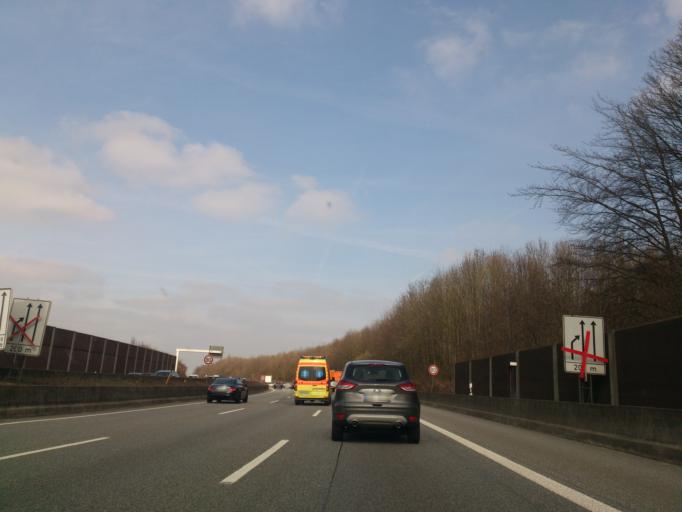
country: DE
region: North Rhine-Westphalia
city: Haan
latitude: 51.2126
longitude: 7.0536
